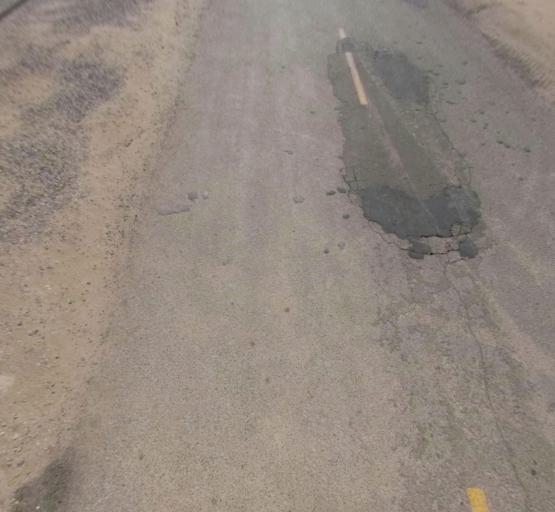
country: US
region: California
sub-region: Madera County
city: Chowchilla
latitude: 37.0908
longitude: -120.2782
